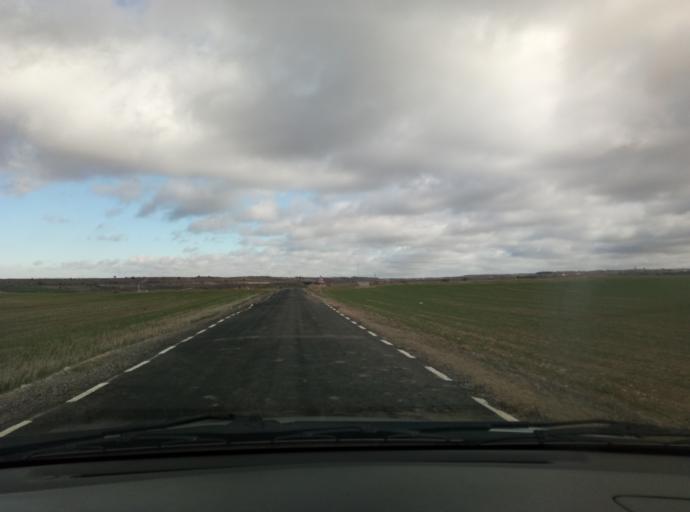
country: ES
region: Catalonia
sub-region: Provincia de Lleida
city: Verdu
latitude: 41.5990
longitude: 1.0995
